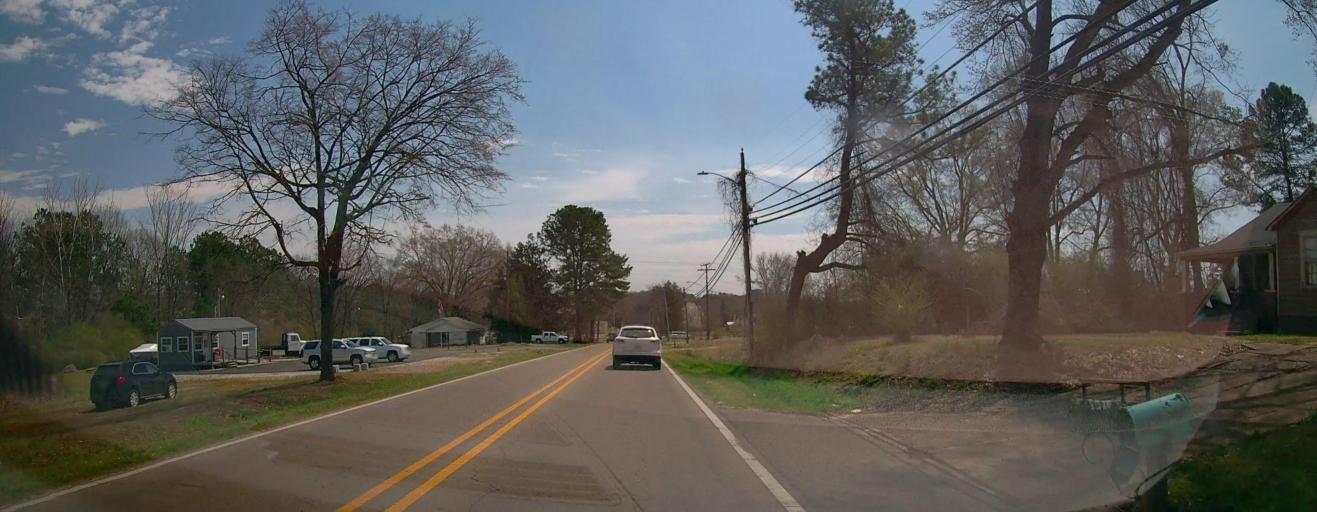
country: US
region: Mississippi
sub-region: Union County
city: New Albany
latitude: 34.4761
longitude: -88.9961
